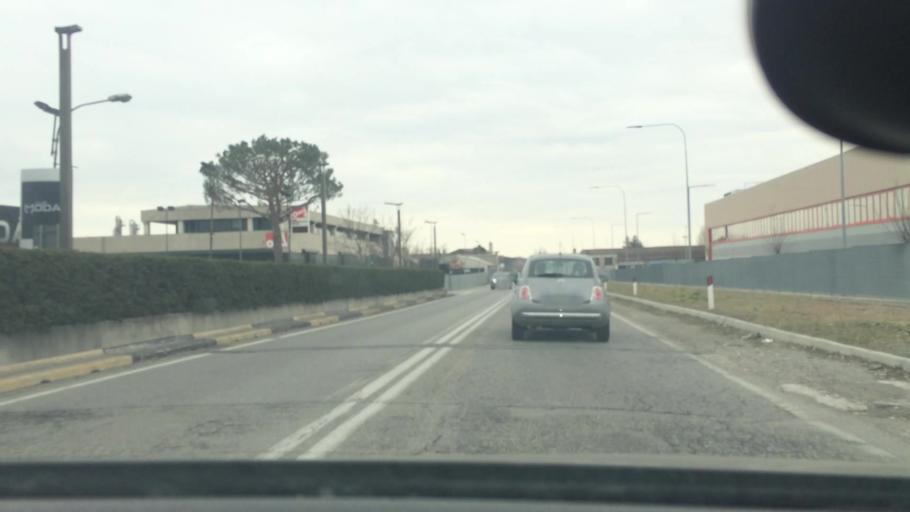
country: IT
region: Lombardy
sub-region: Provincia di Como
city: Merone
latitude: 45.7983
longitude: 9.2394
